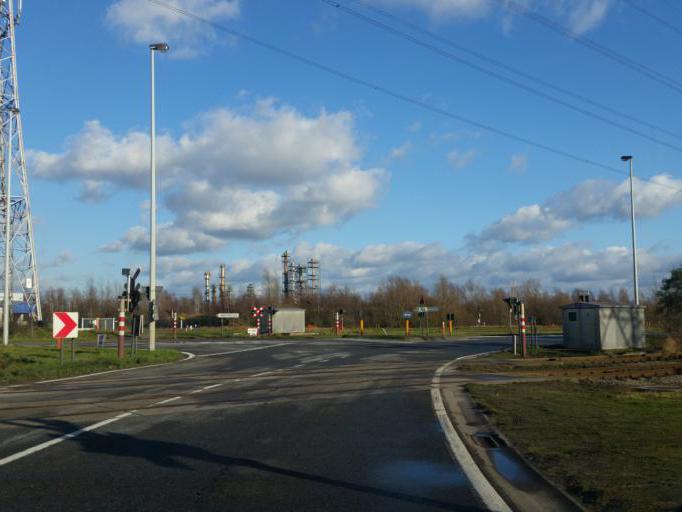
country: BE
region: Flanders
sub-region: Provincie Oost-Vlaanderen
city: Beveren
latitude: 51.2873
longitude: 4.2803
